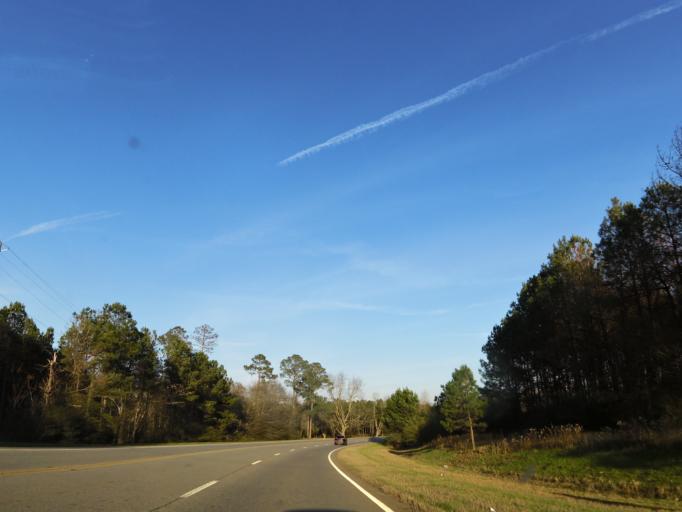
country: US
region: Georgia
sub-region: Sumter County
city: Americus
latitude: 32.0558
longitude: -84.3214
